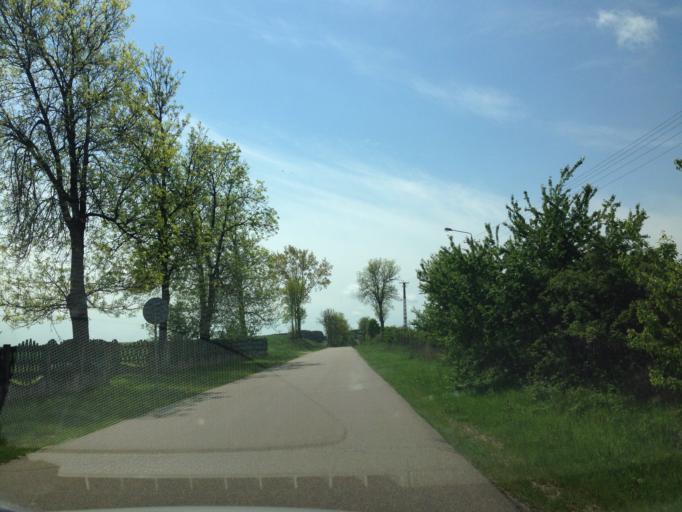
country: PL
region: Podlasie
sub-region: Powiat lomzynski
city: Wizna
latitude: 53.2764
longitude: 22.4540
